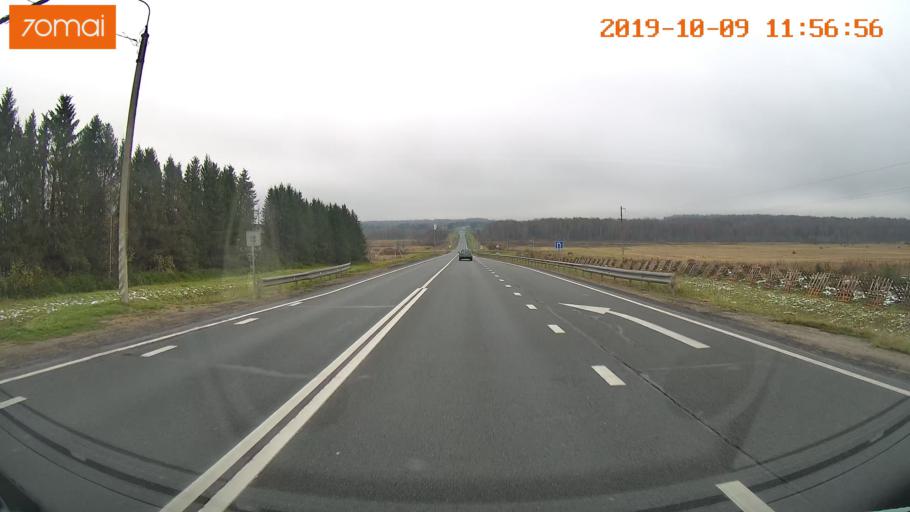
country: RU
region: Vologda
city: Gryazovets
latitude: 58.7386
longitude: 40.2899
